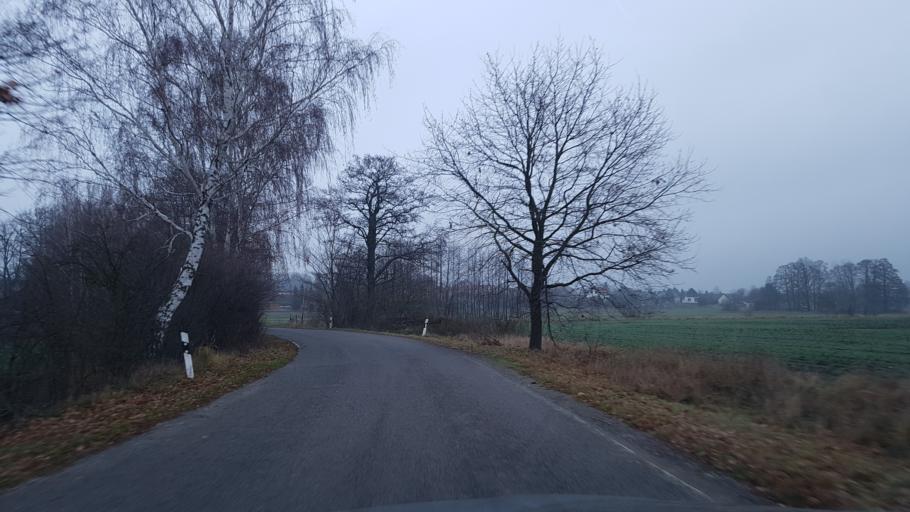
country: DE
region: Brandenburg
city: Ruckersdorf
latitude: 51.5512
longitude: 13.5894
